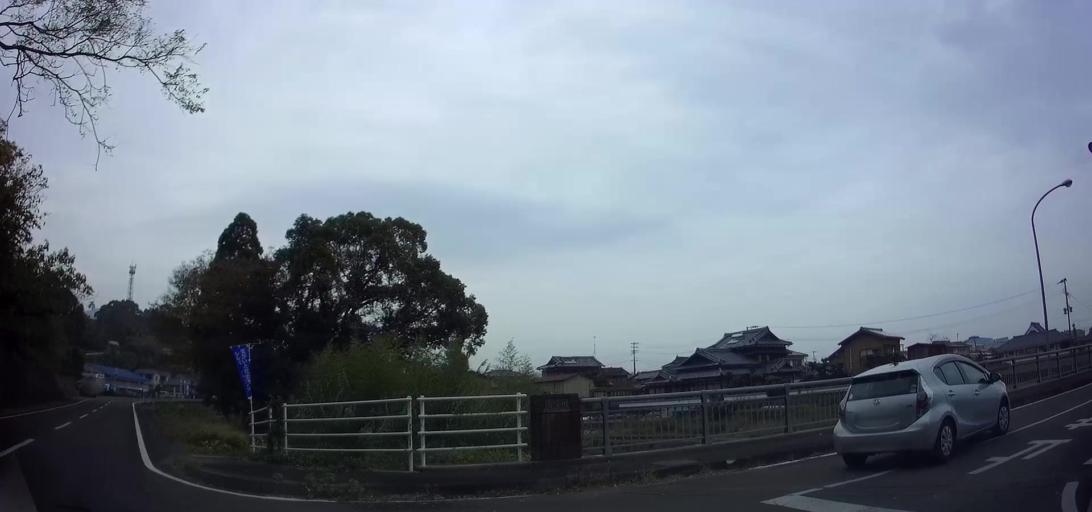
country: JP
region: Nagasaki
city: Shimabara
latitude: 32.6669
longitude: 130.2984
